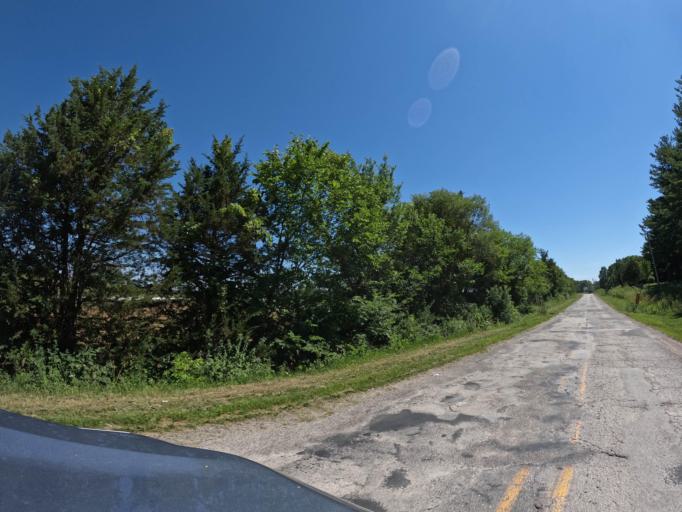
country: US
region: Iowa
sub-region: Monroe County
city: Albia
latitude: 41.0272
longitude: -92.7765
